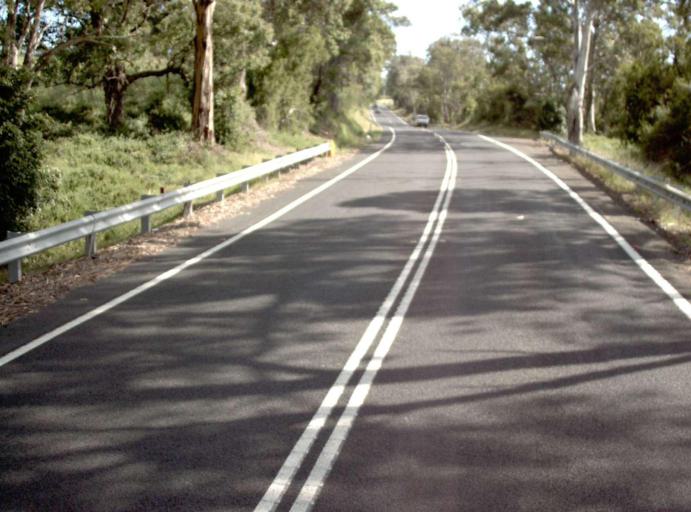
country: AU
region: Victoria
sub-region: East Gippsland
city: Lakes Entrance
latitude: -37.8554
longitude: 148.0308
